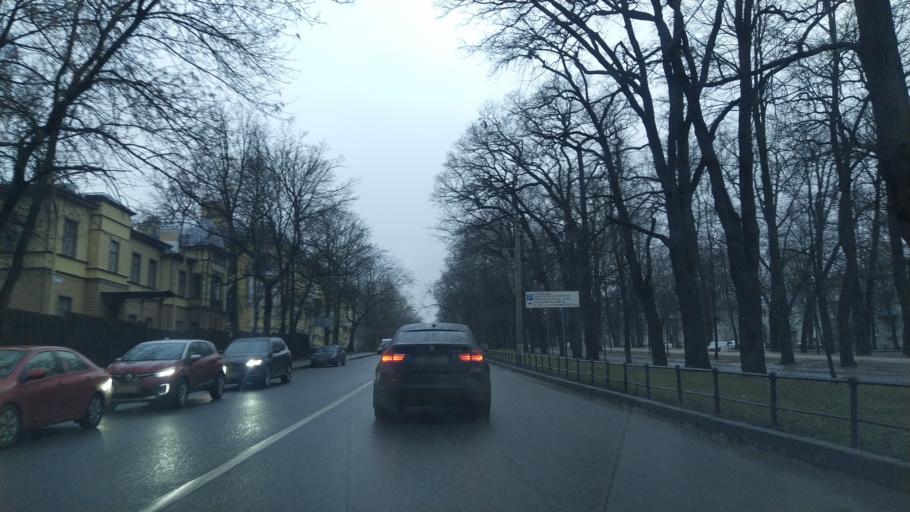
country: RU
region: St.-Petersburg
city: Pushkin
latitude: 59.7194
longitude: 30.4237
